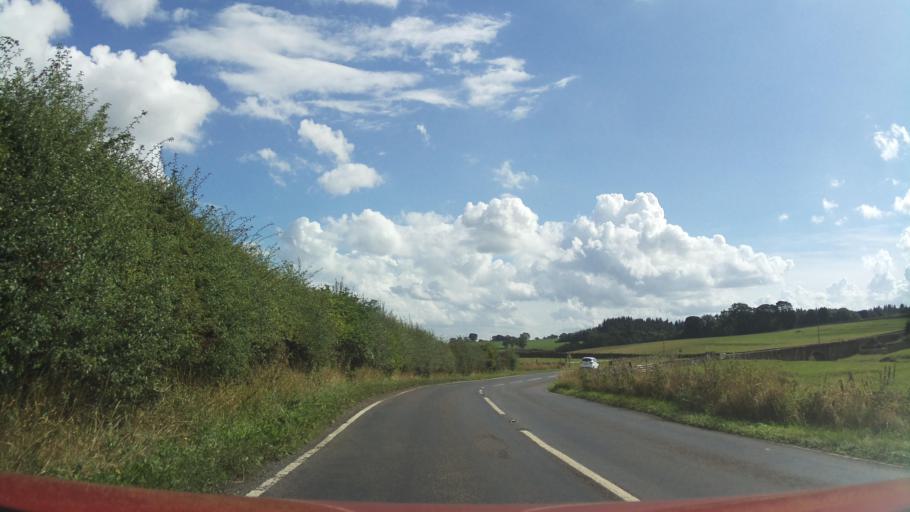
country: GB
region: England
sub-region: North Yorkshire
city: Leyburn
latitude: 54.3609
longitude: -1.8179
